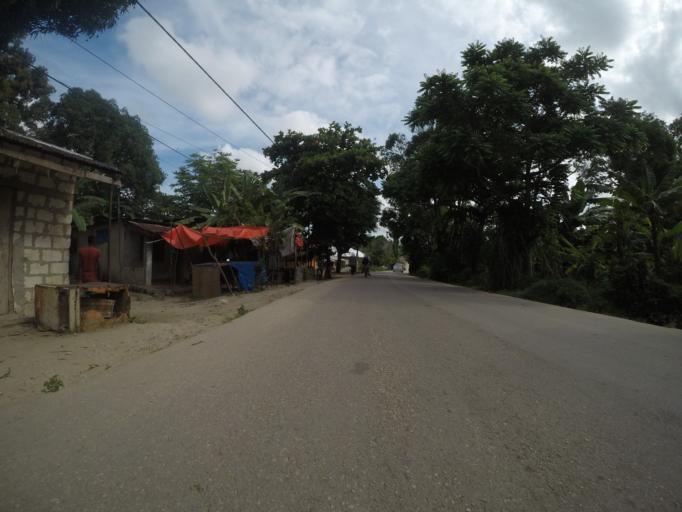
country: TZ
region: Pemba South
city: Chake Chake
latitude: -5.2418
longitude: 39.7822
